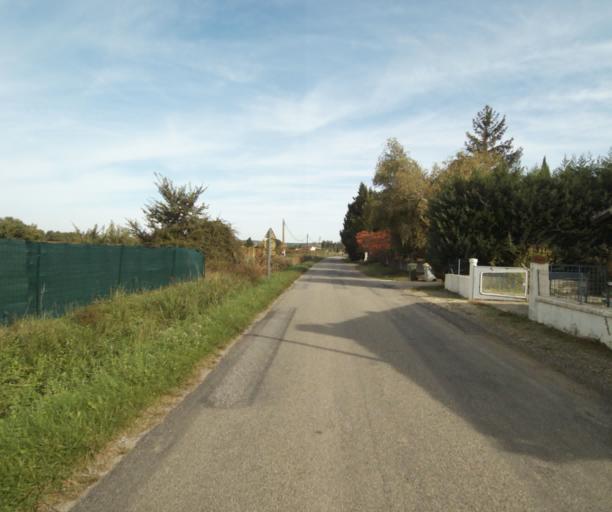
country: FR
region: Midi-Pyrenees
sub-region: Departement du Tarn-et-Garonne
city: Orgueil
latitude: 43.8981
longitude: 1.4094
